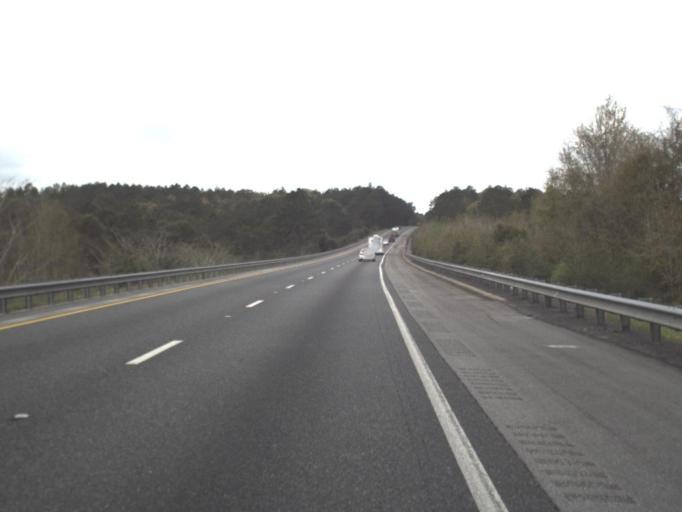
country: US
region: Florida
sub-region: Okaloosa County
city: Crestview
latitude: 30.7149
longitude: -86.6198
